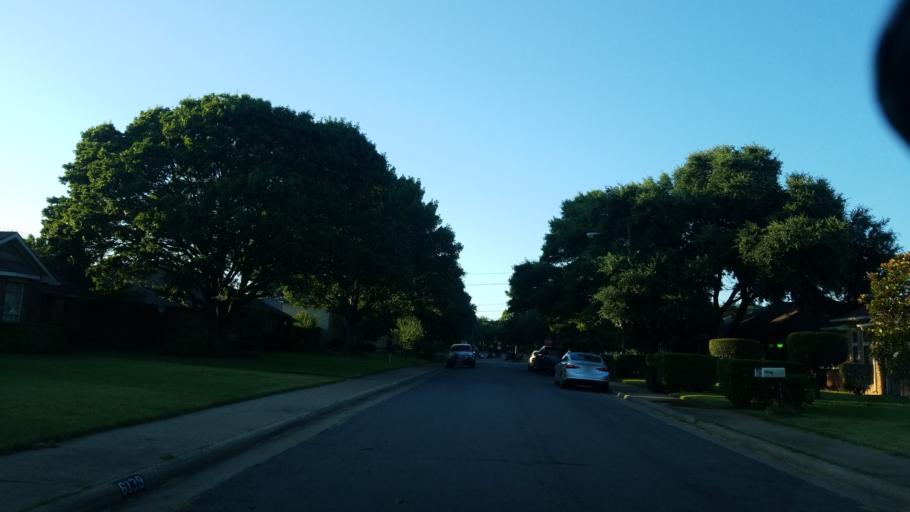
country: US
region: Texas
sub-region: Dallas County
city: Balch Springs
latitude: 32.7877
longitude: -96.6976
